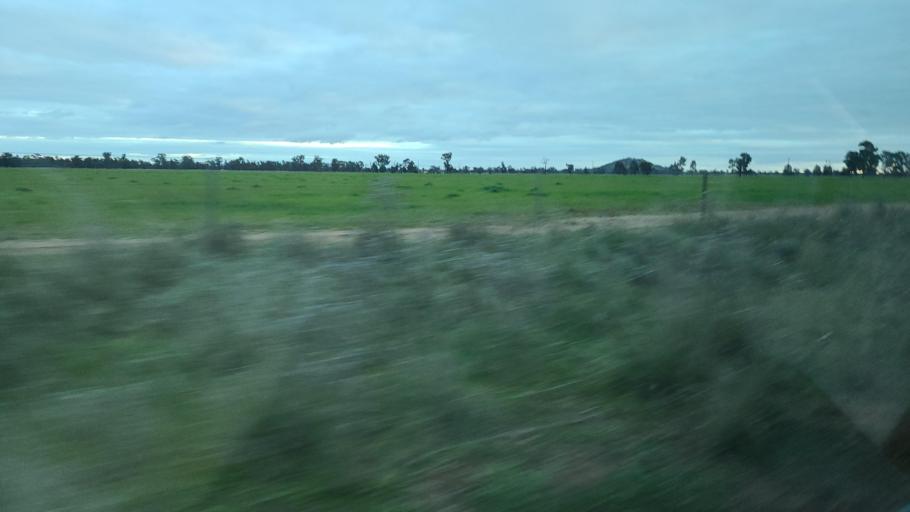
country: AU
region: New South Wales
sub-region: Coolamon
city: Coolamon
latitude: -34.8542
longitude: 146.9042
